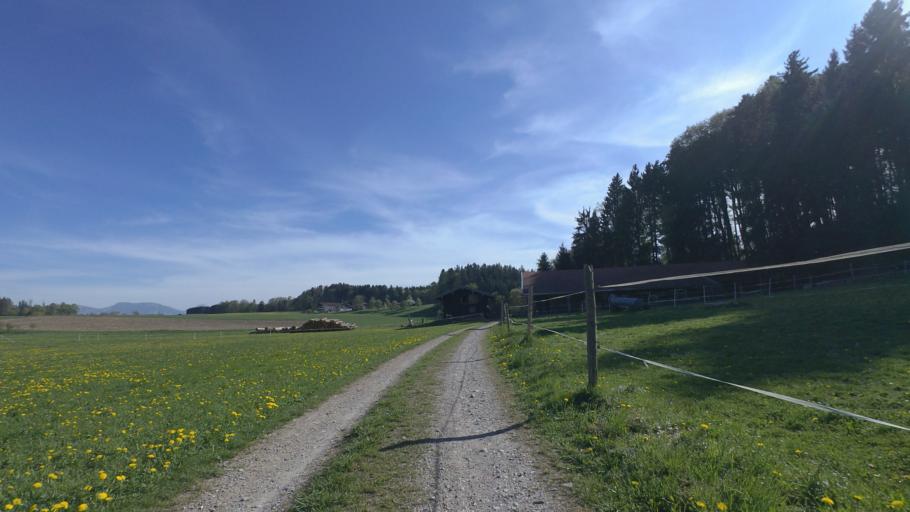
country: DE
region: Bavaria
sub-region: Upper Bavaria
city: Grabenstatt
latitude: 47.8642
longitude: 12.5702
